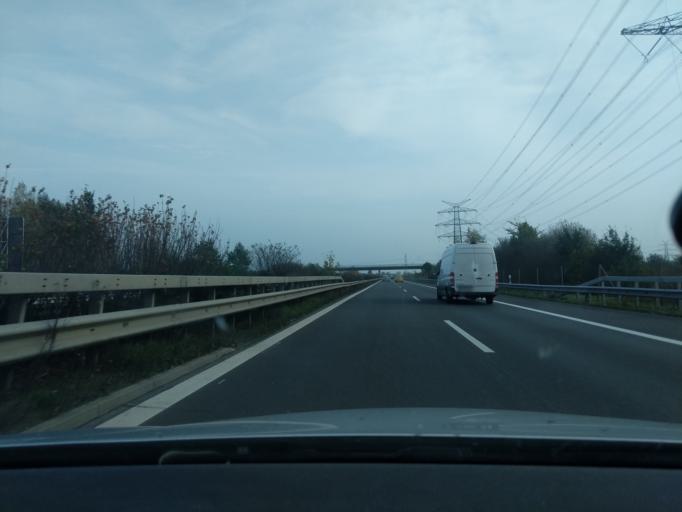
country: DE
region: Lower Saxony
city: Agathenburg
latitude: 53.5741
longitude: 9.5401
